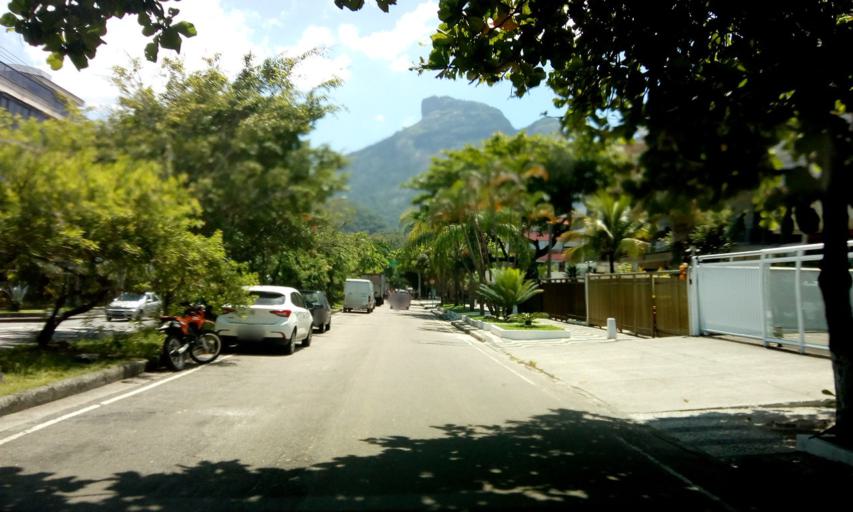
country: BR
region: Rio de Janeiro
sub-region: Rio De Janeiro
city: Rio de Janeiro
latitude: -23.0134
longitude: -43.3128
